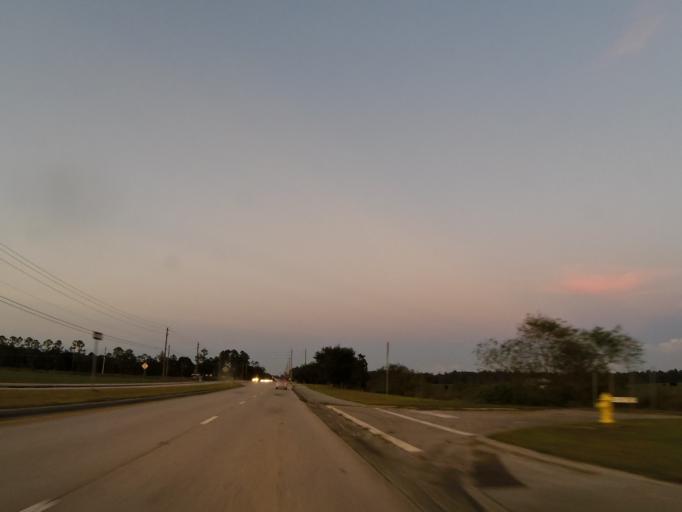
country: US
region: Florida
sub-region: Saint Johns County
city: Saint Augustine
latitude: 29.9673
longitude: -81.4864
